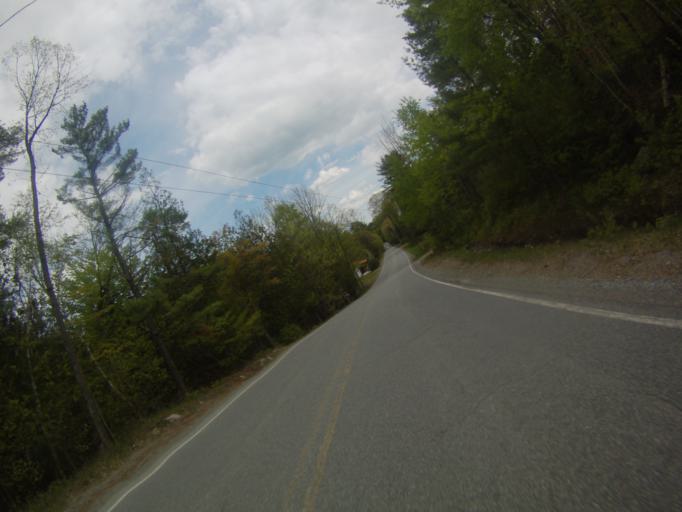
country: US
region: New York
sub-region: Essex County
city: Port Henry
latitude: 43.9452
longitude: -73.4881
